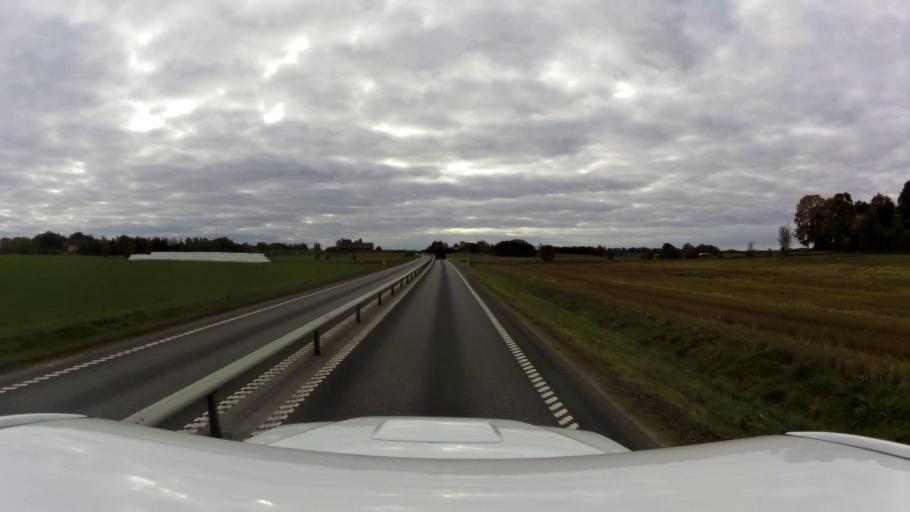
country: SE
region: OEstergoetland
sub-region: Linkopings Kommun
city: Malmslatt
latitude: 58.3402
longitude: 15.5547
